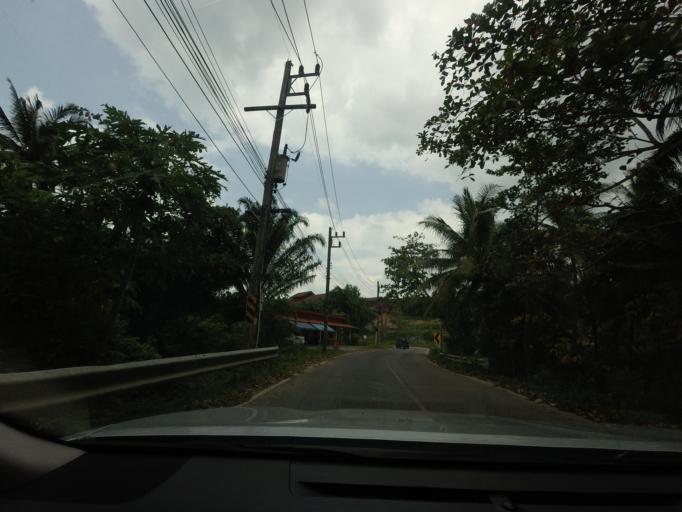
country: TH
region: Phangnga
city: Ban Ao Nang
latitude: 8.0751
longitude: 98.7460
